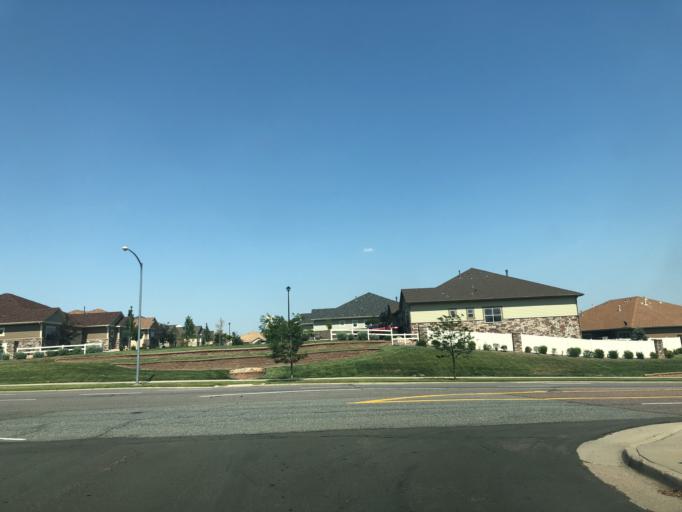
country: US
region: Colorado
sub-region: Arapahoe County
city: Dove Valley
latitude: 39.6361
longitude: -104.7634
